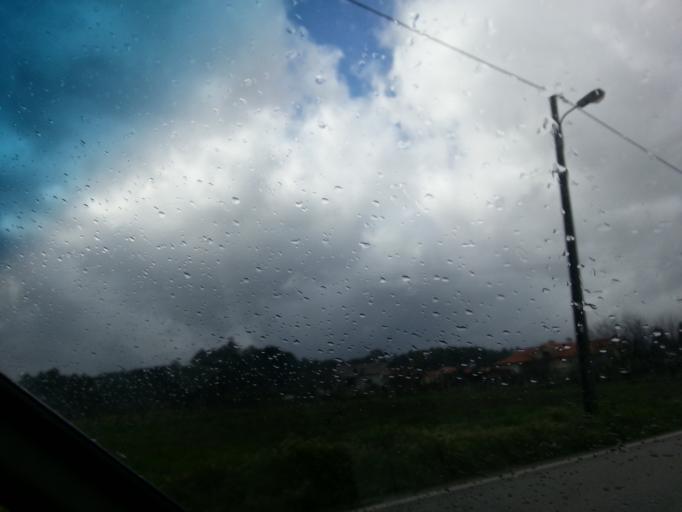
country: PT
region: Viseu
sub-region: Viseu
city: Rio de Loba
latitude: 40.6339
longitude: -7.8660
